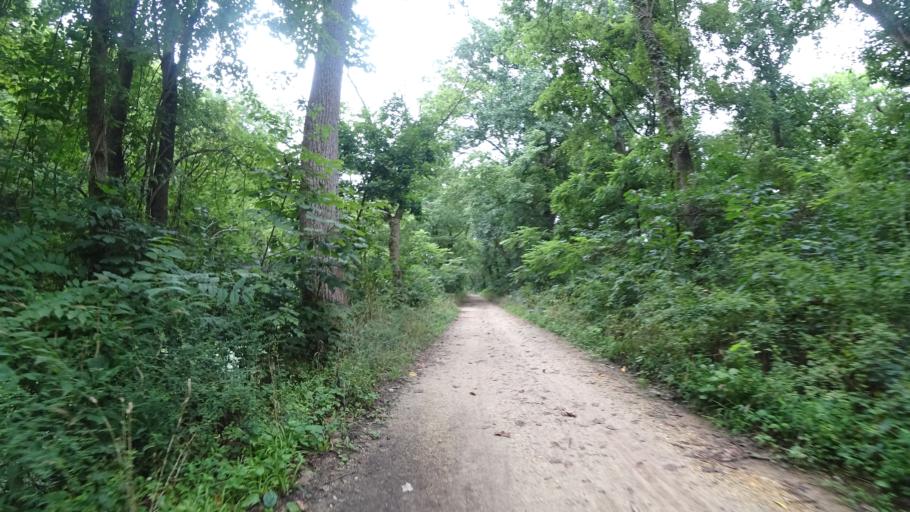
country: US
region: Virginia
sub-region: Loudoun County
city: Lowes Island
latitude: 39.0681
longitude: -77.3499
